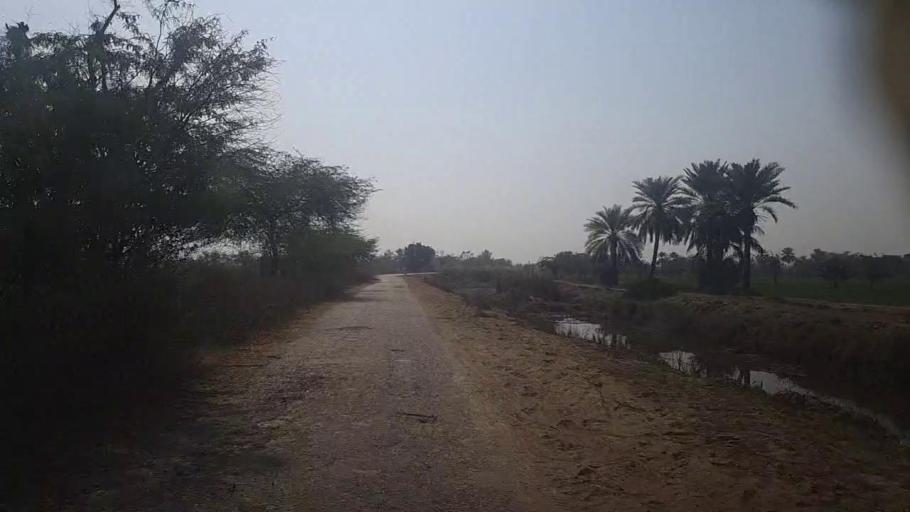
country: PK
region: Sindh
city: Kot Diji
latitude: 27.4151
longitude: 68.7949
